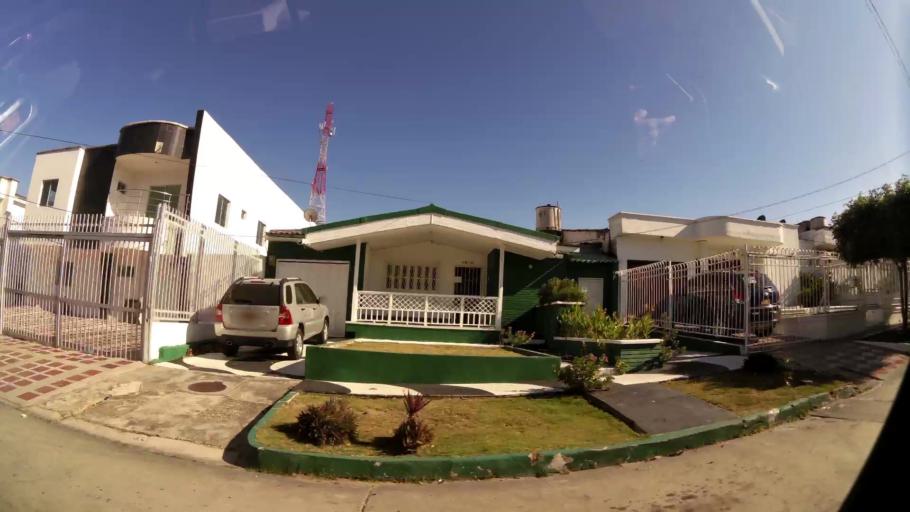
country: CO
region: Atlantico
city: Barranquilla
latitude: 10.9961
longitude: -74.8279
